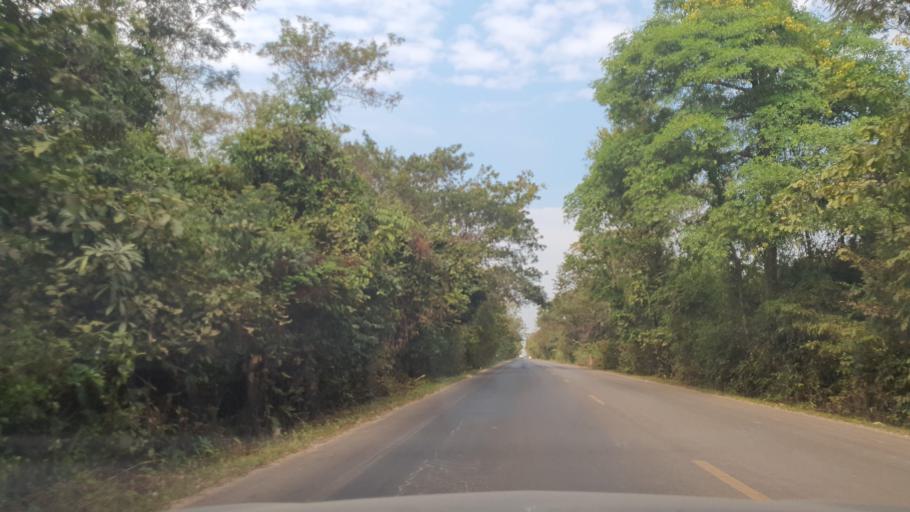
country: TH
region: Changwat Bueng Kan
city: Si Wilai
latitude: 18.2877
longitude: 103.8245
